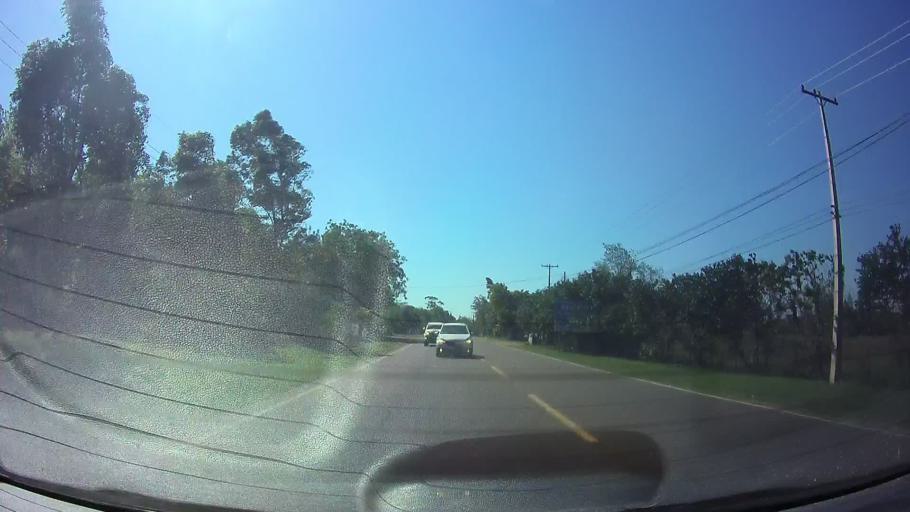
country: PY
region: Cordillera
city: San Bernardino
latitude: -25.3452
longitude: -57.2727
